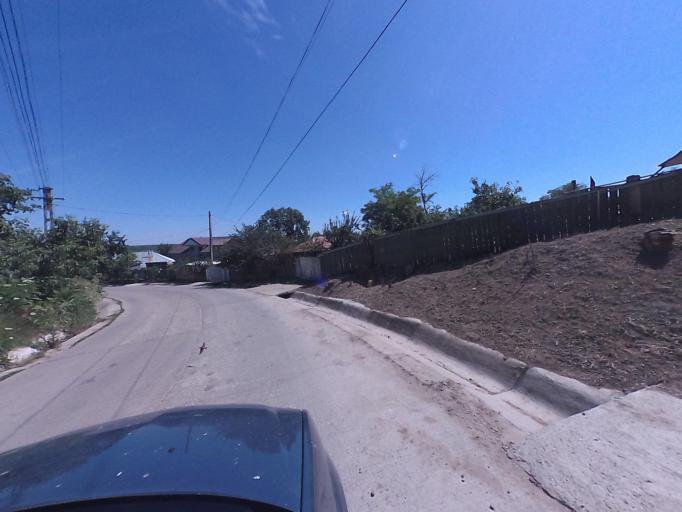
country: RO
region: Vaslui
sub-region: Comuna Costesti
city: Costesti
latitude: 46.4898
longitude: 27.7689
